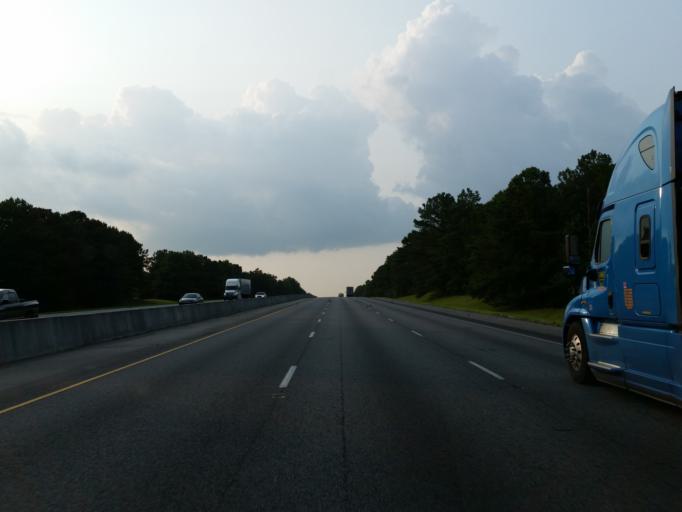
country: US
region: Georgia
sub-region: Bibb County
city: West Point
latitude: 32.9276
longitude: -83.8031
